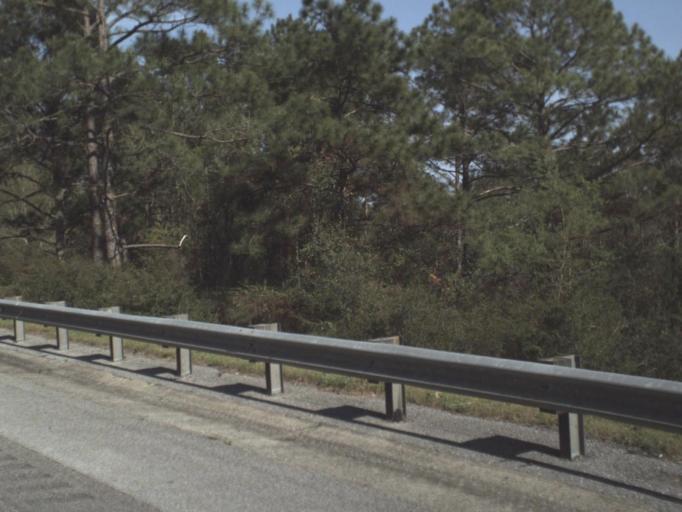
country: US
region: Florida
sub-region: Okaloosa County
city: Crestview
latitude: 30.7193
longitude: -86.4280
